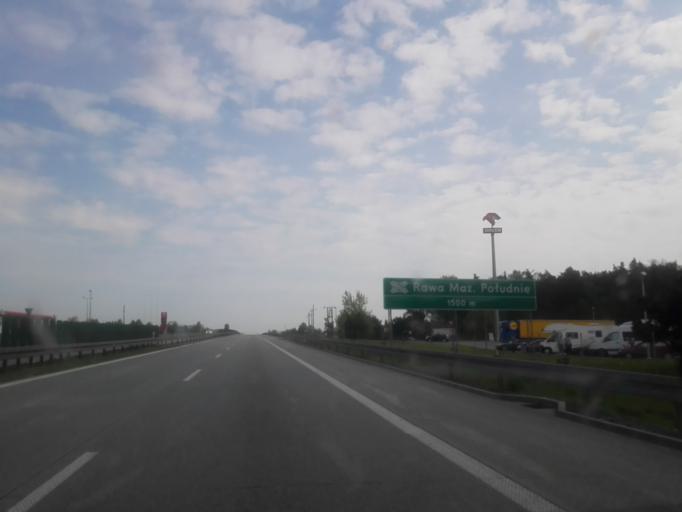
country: PL
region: Lodz Voivodeship
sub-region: Powiat rawski
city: Rawa Mazowiecka
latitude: 51.7344
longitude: 20.2311
